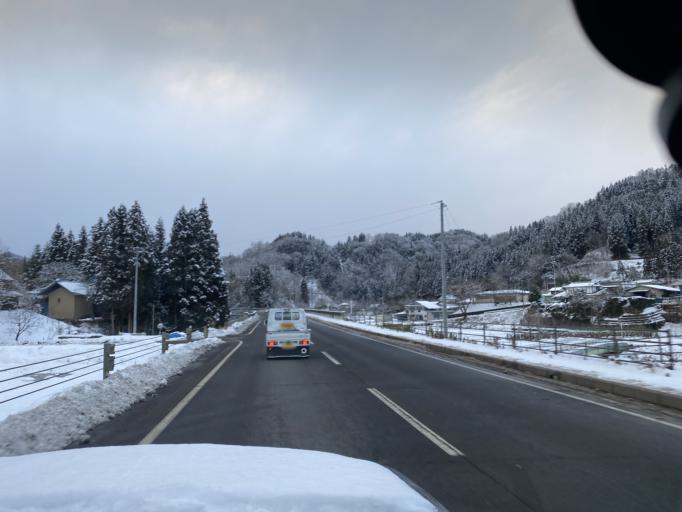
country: JP
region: Nagano
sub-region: Kitaazumi Gun
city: Hakuba
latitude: 36.6049
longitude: 138.0075
